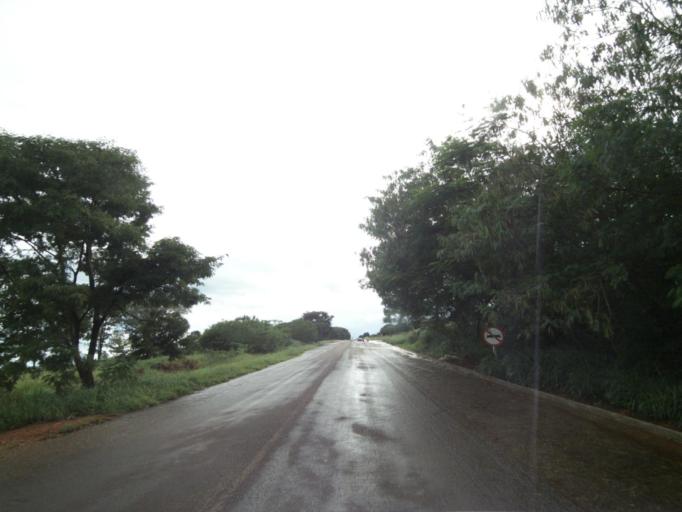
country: BR
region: Goias
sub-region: Itaberai
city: Itaberai
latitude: -15.9178
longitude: -49.5954
